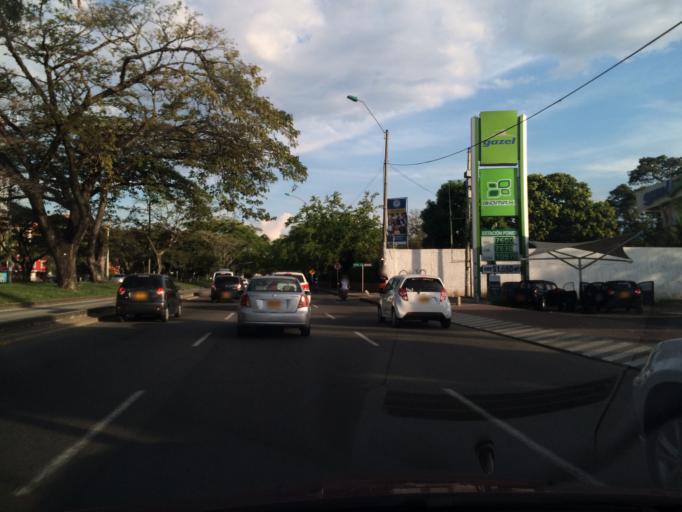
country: CO
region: Valle del Cauca
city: Cali
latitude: 3.3802
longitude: -76.5437
